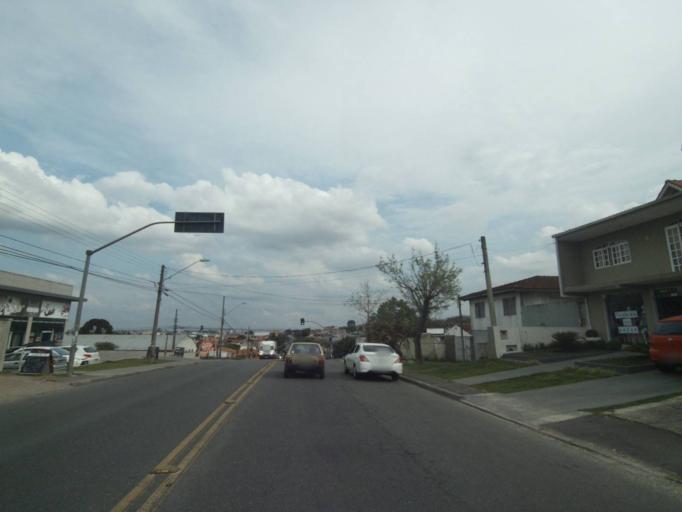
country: BR
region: Parana
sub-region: Pinhais
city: Pinhais
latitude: -25.4119
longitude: -49.2066
